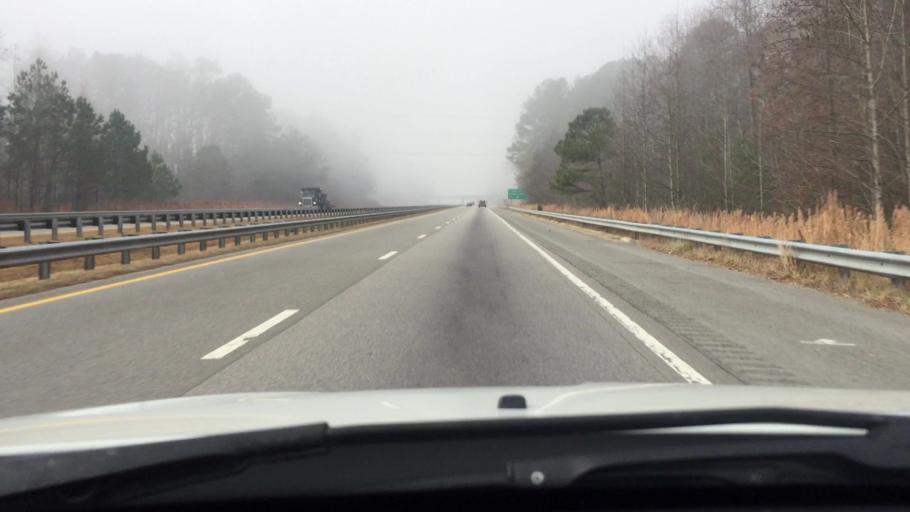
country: US
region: North Carolina
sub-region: Wake County
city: Holly Springs
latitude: 35.6715
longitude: -78.9245
